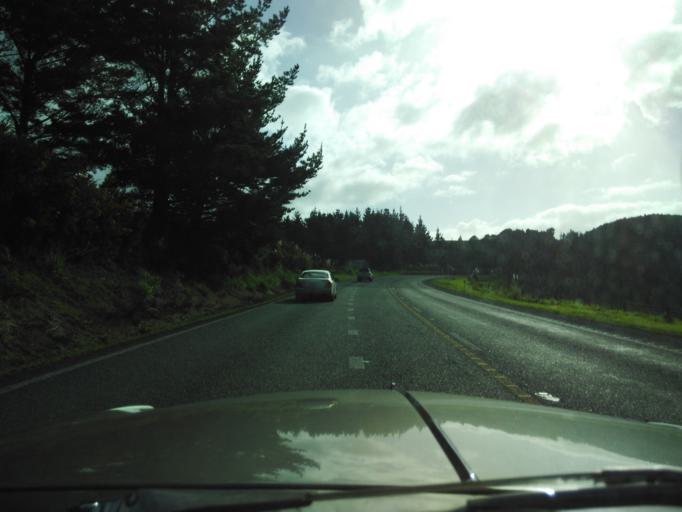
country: NZ
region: Auckland
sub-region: Auckland
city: Wellsford
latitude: -36.1918
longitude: 174.4521
